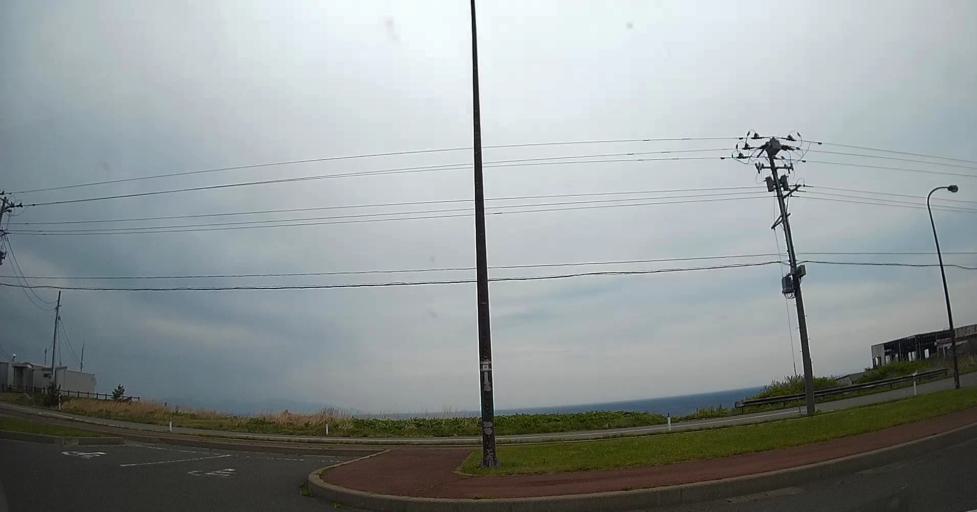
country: JP
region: Aomori
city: Shimokizukuri
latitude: 41.2575
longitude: 140.3452
